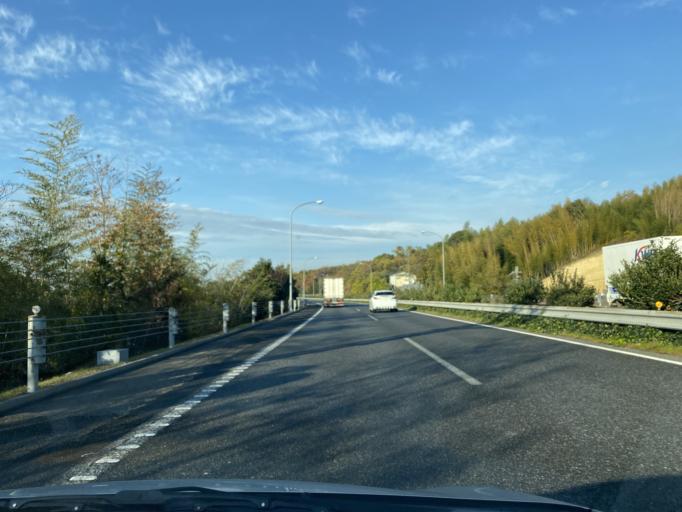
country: JP
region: Osaka
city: Izumi
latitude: 34.4221
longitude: 135.4482
